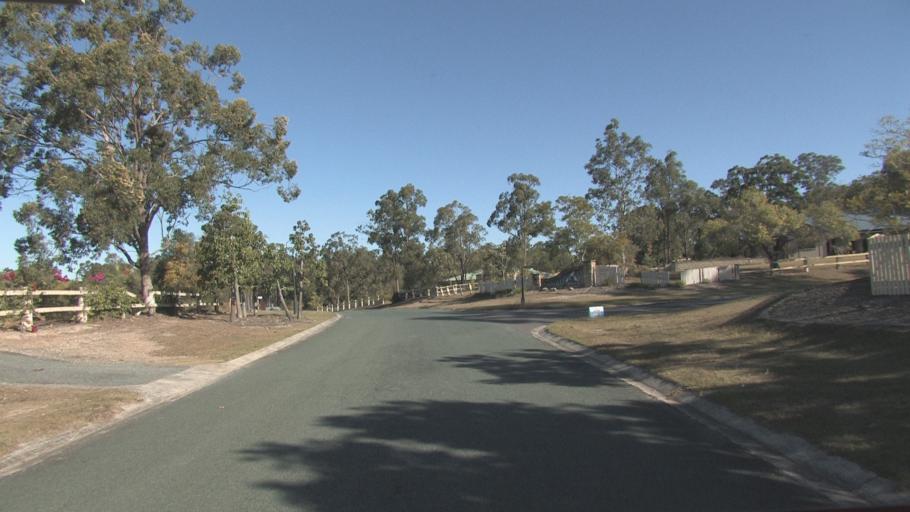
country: AU
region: Queensland
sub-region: Ipswich
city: Springfield Lakes
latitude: -27.7265
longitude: 152.9226
